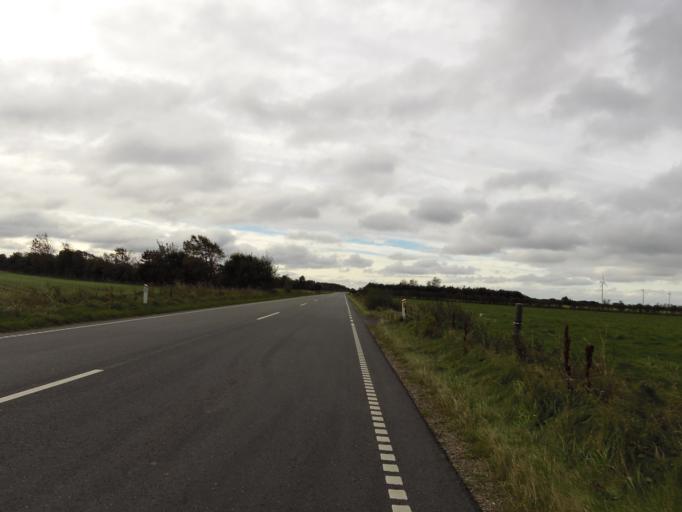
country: DK
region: South Denmark
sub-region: Tonder Kommune
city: Sherrebek
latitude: 55.2067
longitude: 8.7967
